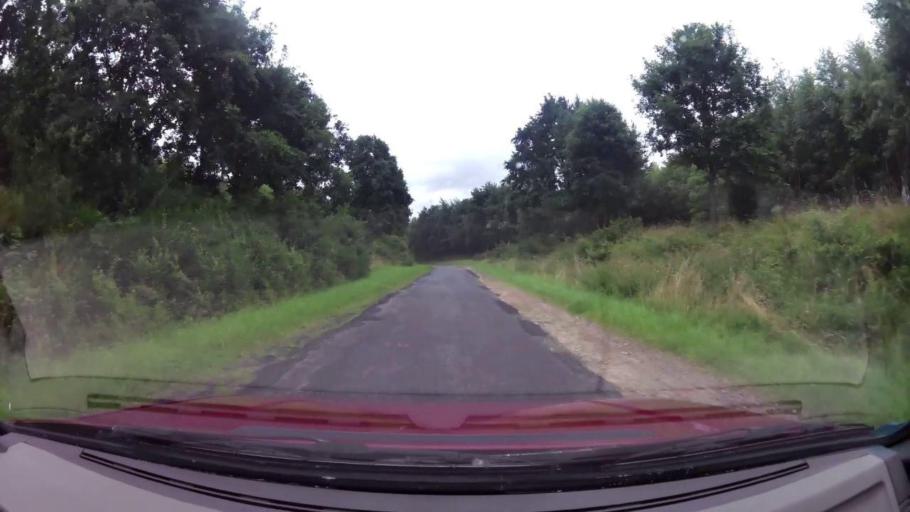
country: PL
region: West Pomeranian Voivodeship
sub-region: Powiat swidwinski
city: Rabino
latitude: 53.9339
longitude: 15.9625
